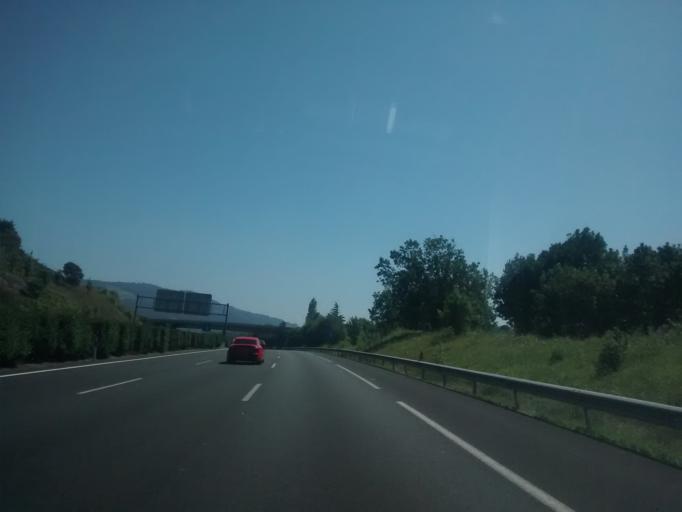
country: ES
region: Cantabria
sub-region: Provincia de Cantabria
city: Entrambasaguas
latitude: 43.3873
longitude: -3.6766
